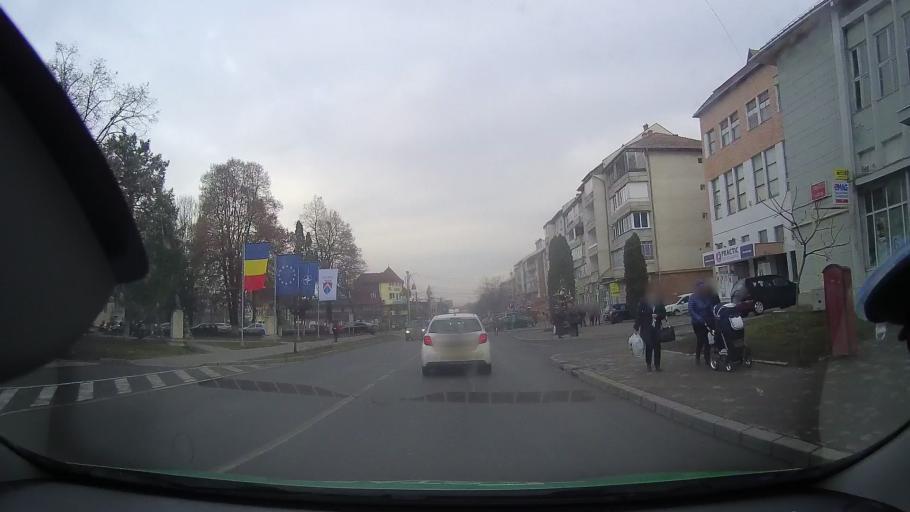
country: RO
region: Mures
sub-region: Comuna Ludus
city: Ludus
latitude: 46.4745
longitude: 24.0954
